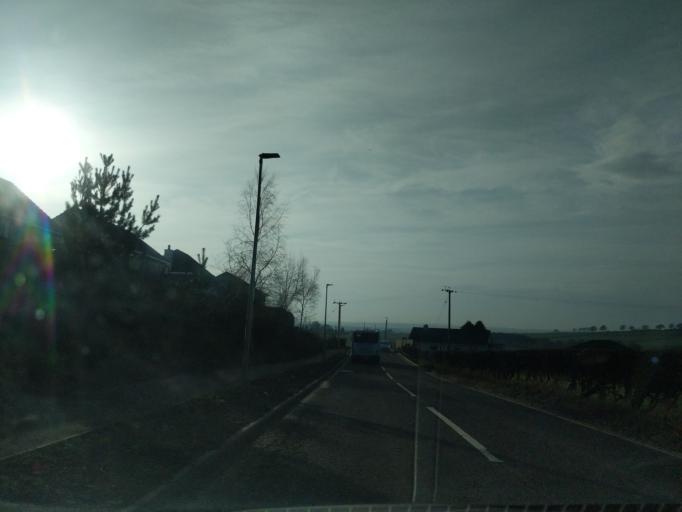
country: GB
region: Scotland
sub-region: South Lanarkshire
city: Carluke
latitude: 55.7381
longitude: -3.8570
